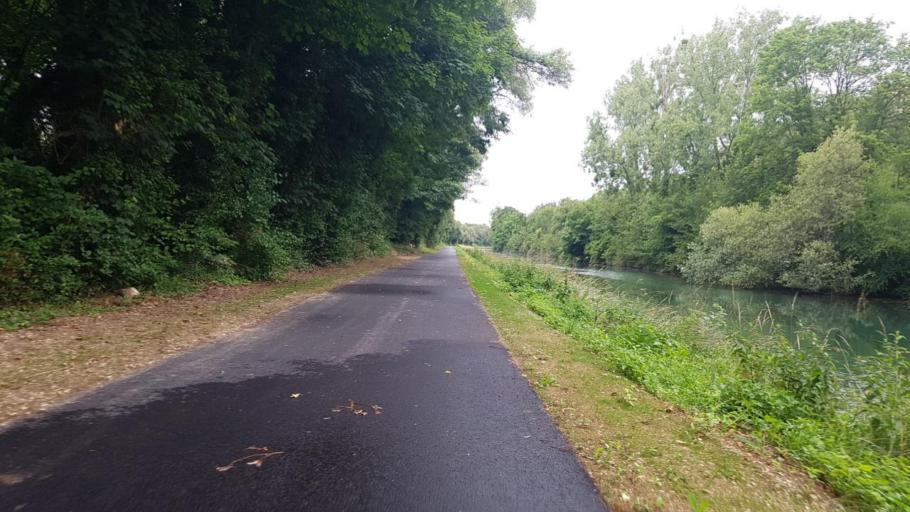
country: FR
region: Champagne-Ardenne
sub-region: Departement de la Marne
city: Vitry-le-Francois
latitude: 48.7734
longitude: 4.5478
